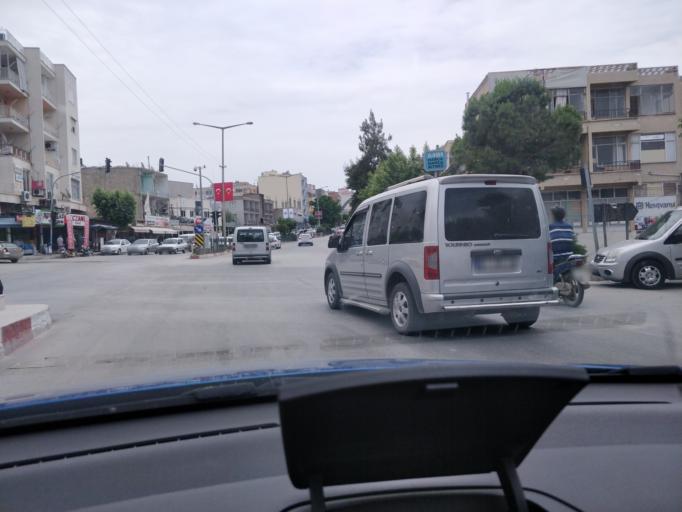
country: TR
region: Mersin
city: Mut
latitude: 36.6463
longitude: 33.4352
